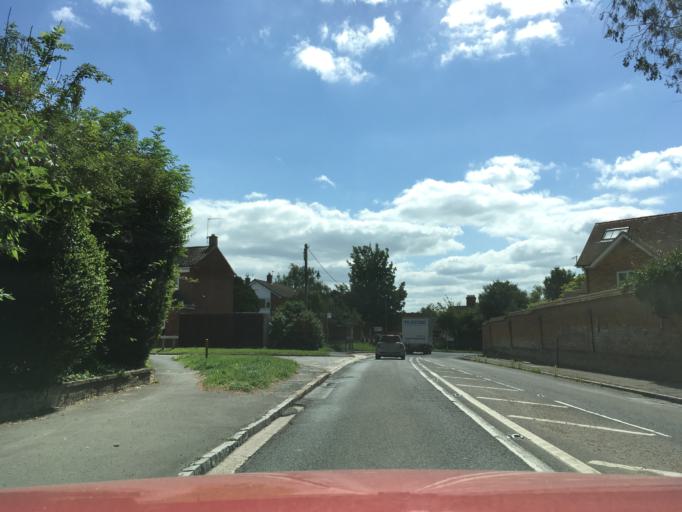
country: GB
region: England
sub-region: Buckinghamshire
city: Aylesbury
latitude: 51.8771
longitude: -0.8325
